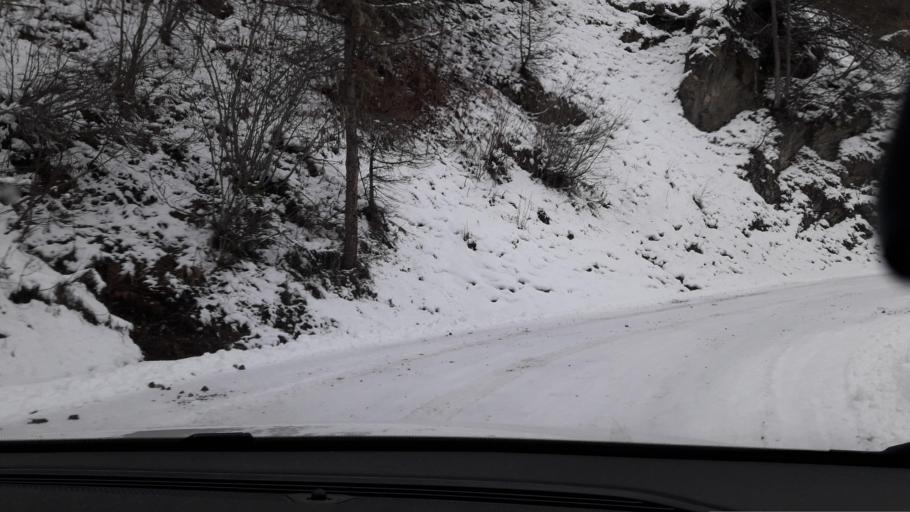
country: FR
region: Rhone-Alpes
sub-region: Departement de la Savoie
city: Valloire
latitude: 45.1992
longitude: 6.4163
